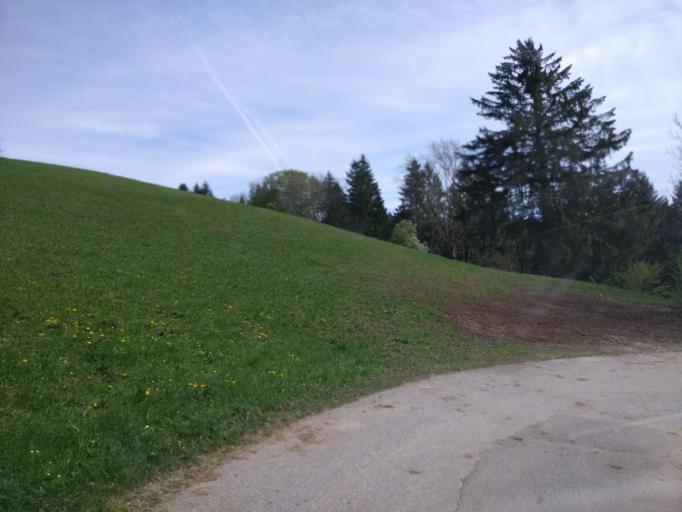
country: AT
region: Salzburg
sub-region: Politischer Bezirk Sankt Johann im Pongau
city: Pfarrwerfen
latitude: 47.4723
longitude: 13.2123
